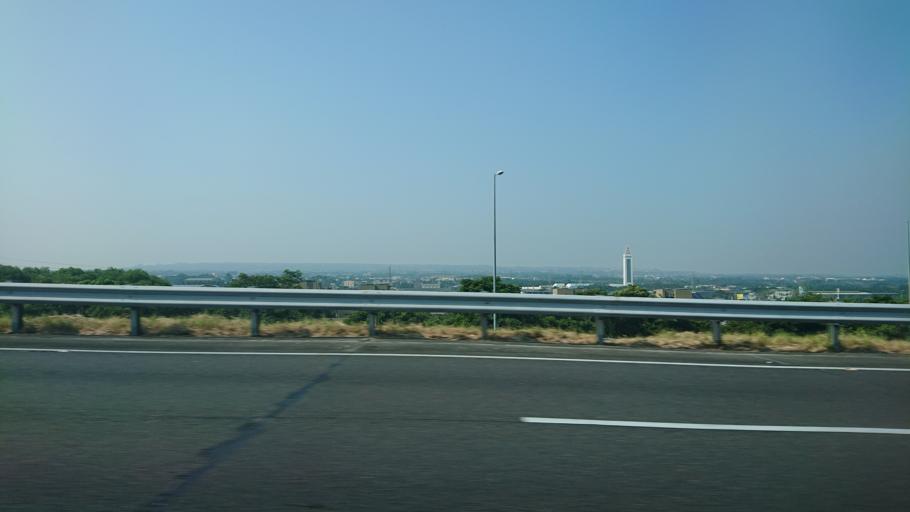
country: TW
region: Taiwan
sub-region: Nantou
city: Nantou
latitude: 23.8502
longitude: 120.7031
